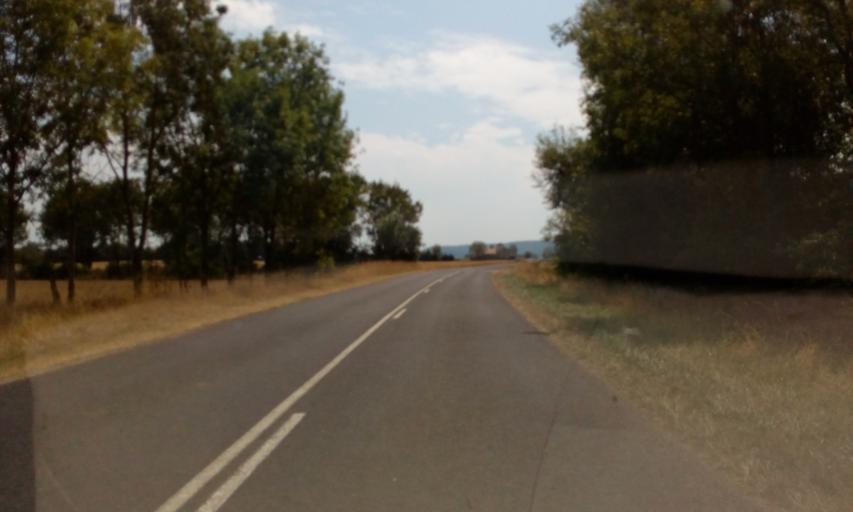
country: FR
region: Lorraine
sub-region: Departement de la Meuse
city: Vigneulles-les-Hattonchatel
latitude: 49.0740
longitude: 5.6443
